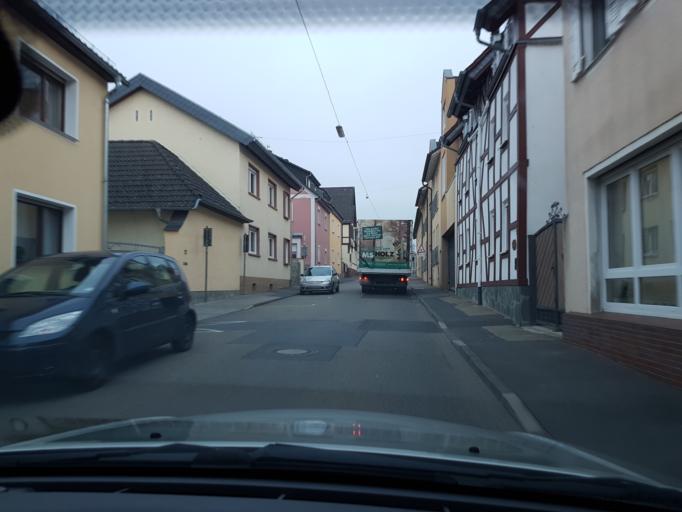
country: DE
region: Hesse
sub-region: Regierungsbezirk Darmstadt
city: Kiedrich
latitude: 50.0220
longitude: 8.0945
